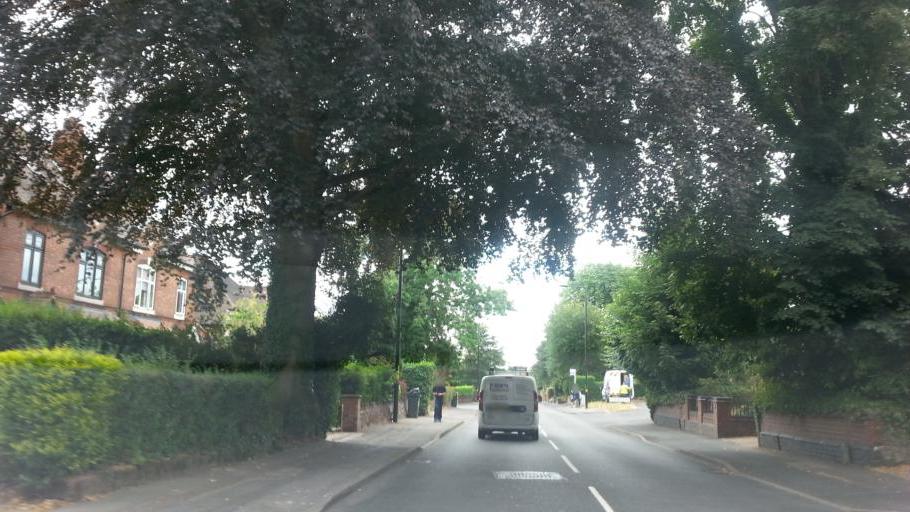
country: GB
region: England
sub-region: City and Borough of Birmingham
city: Sutton Coldfield
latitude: 52.5406
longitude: -1.8374
